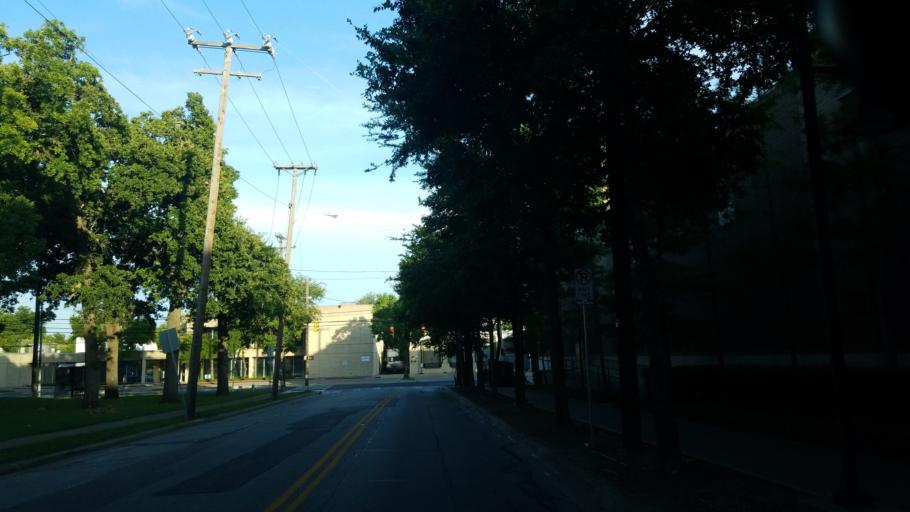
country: US
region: Texas
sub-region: Dallas County
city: Highland Park
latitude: 32.8068
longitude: -96.7887
